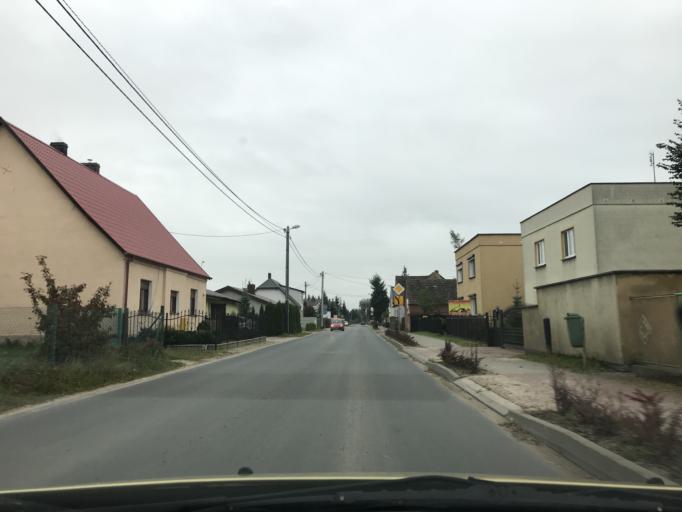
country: PL
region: Greater Poland Voivodeship
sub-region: Powiat poznanski
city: Baranowo
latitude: 52.4028
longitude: 16.7409
